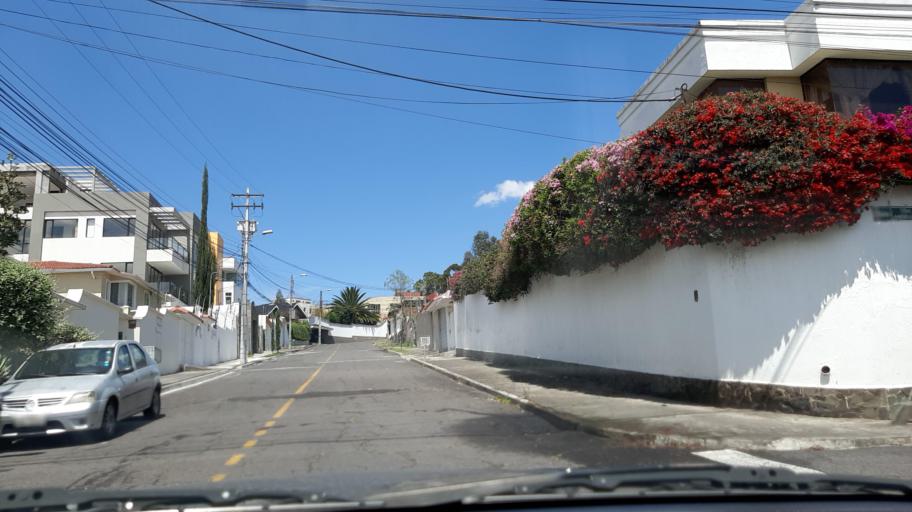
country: EC
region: Pichincha
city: Quito
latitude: -0.2099
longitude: -78.4264
